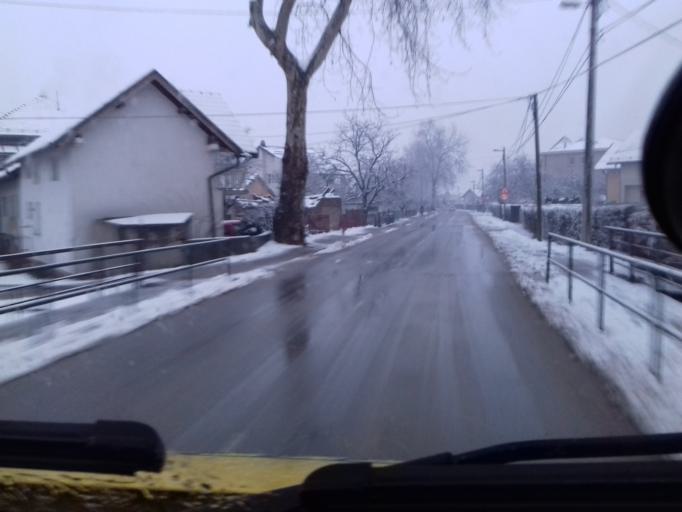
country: BA
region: Federation of Bosnia and Herzegovina
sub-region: Kanton Sarajevo
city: Sarajevo
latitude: 43.8186
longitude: 18.3264
